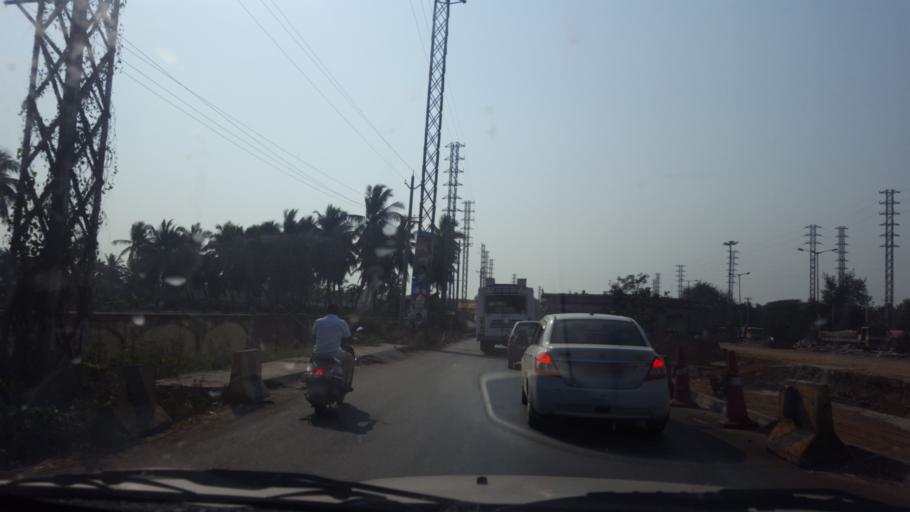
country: IN
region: Andhra Pradesh
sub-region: Vishakhapatnam
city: Anakapalle
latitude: 17.6744
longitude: 83.0026
